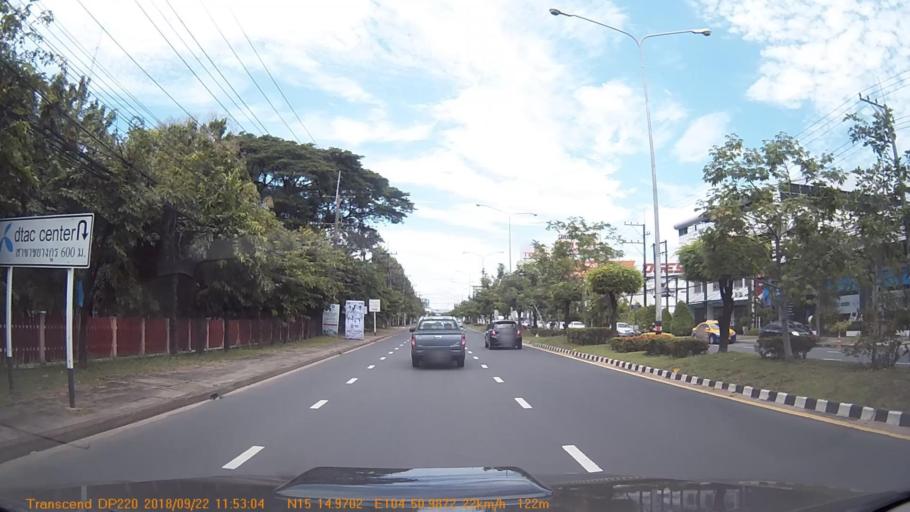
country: TH
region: Changwat Ubon Ratchathani
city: Ubon Ratchathani
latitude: 15.2495
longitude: 104.8498
